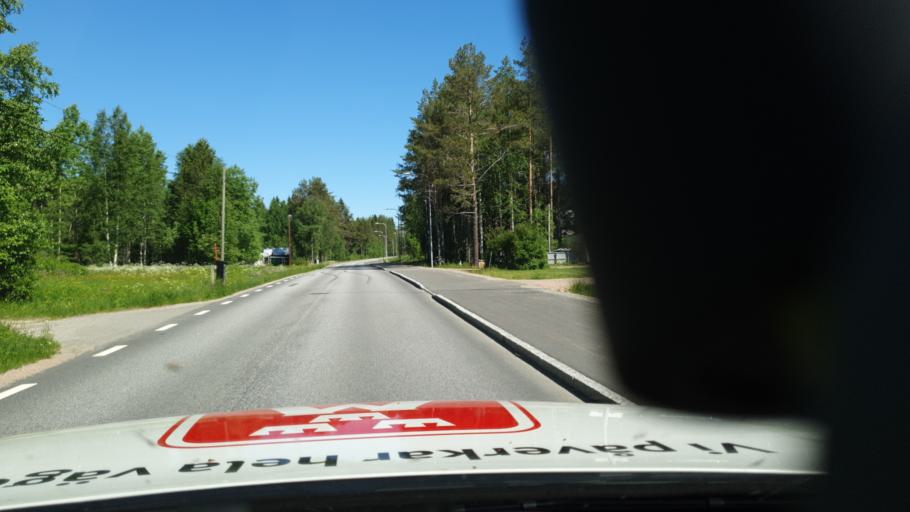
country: SE
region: Jaemtland
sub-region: Bergs Kommun
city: Hoverberg
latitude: 62.4827
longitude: 14.5400
